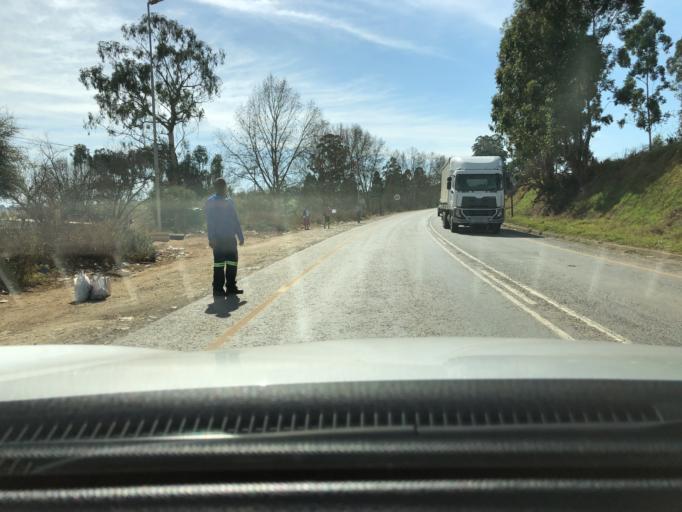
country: ZA
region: KwaZulu-Natal
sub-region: Sisonke District Municipality
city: Ixopo
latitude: -30.1437
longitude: 30.0722
